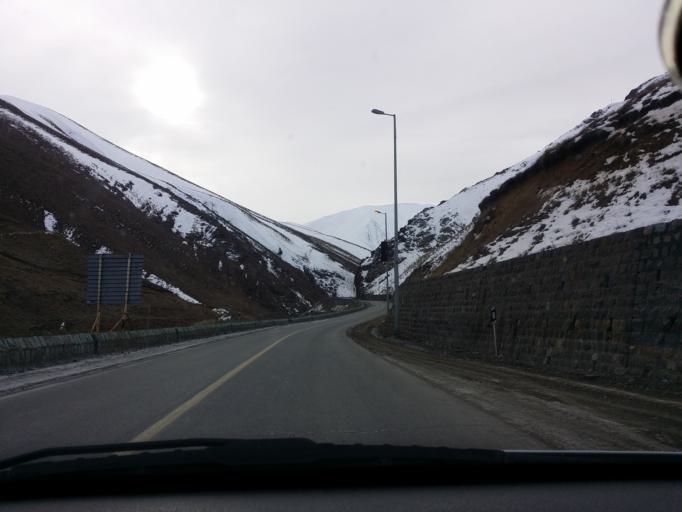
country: IR
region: Tehran
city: Tajrish
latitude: 36.1729
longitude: 51.3145
